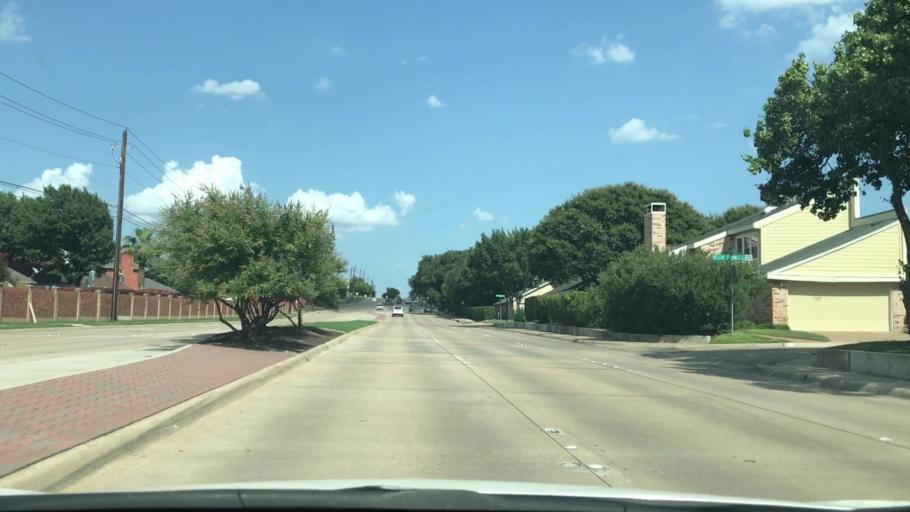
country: US
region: Texas
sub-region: Dallas County
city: Carrollton
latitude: 32.9702
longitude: -96.8637
